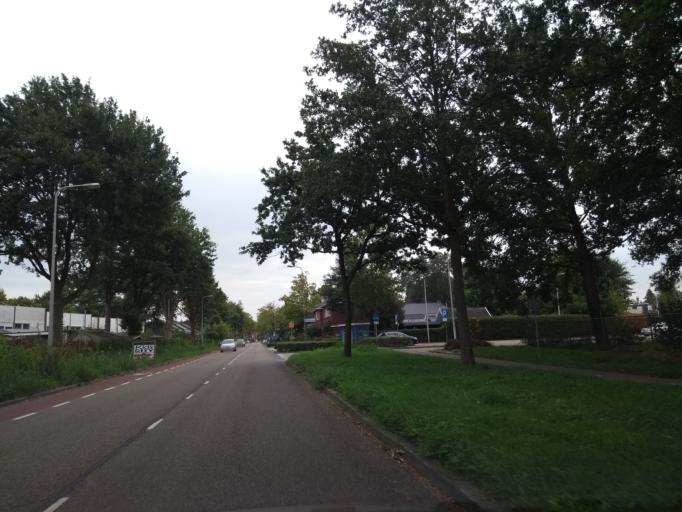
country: NL
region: Overijssel
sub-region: Gemeente Borne
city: Borne
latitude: 52.3026
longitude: 6.7361
